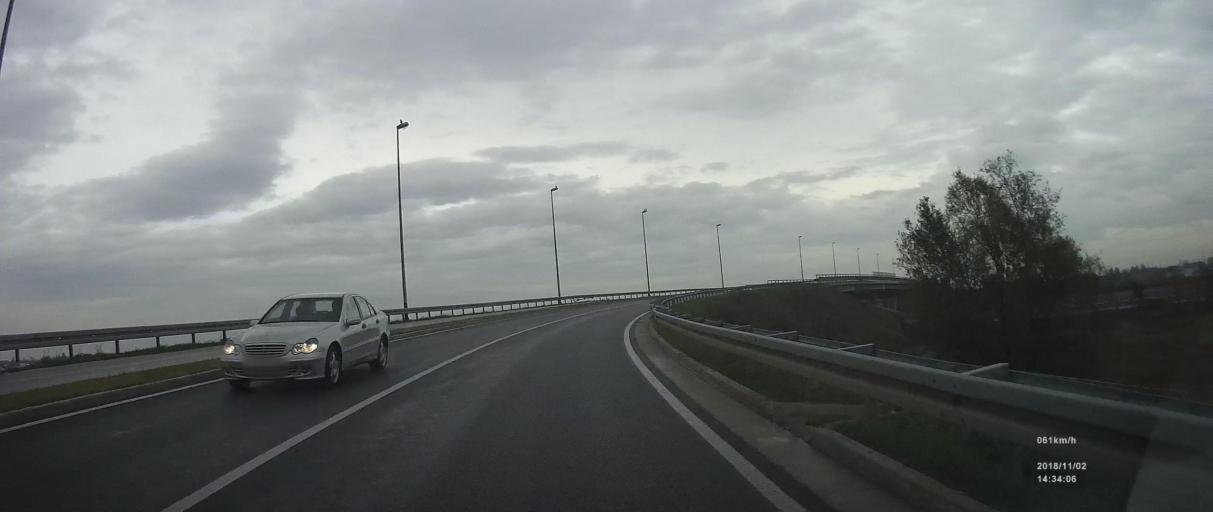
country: HR
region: Zagrebacka
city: Gradici
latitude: 45.6962
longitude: 16.0588
